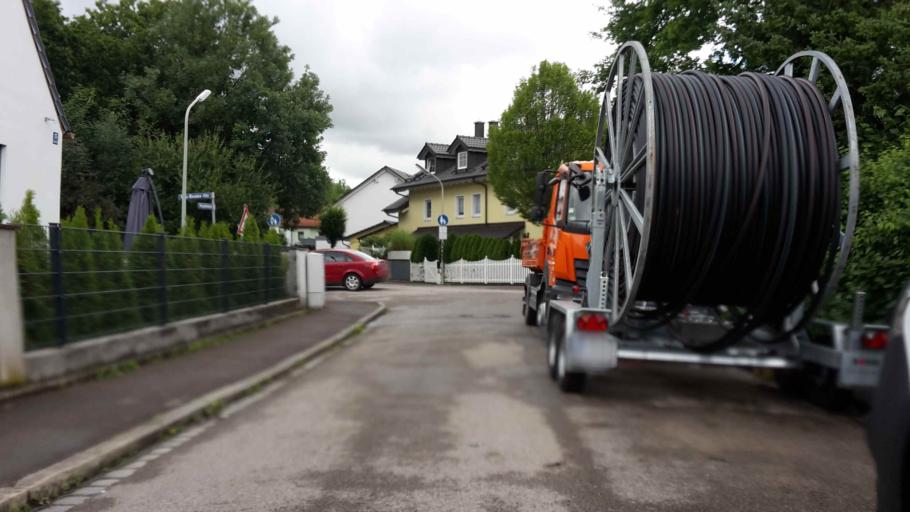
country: DE
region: Bavaria
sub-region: Upper Bavaria
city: Karlsfeld
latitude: 48.1862
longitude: 11.4751
